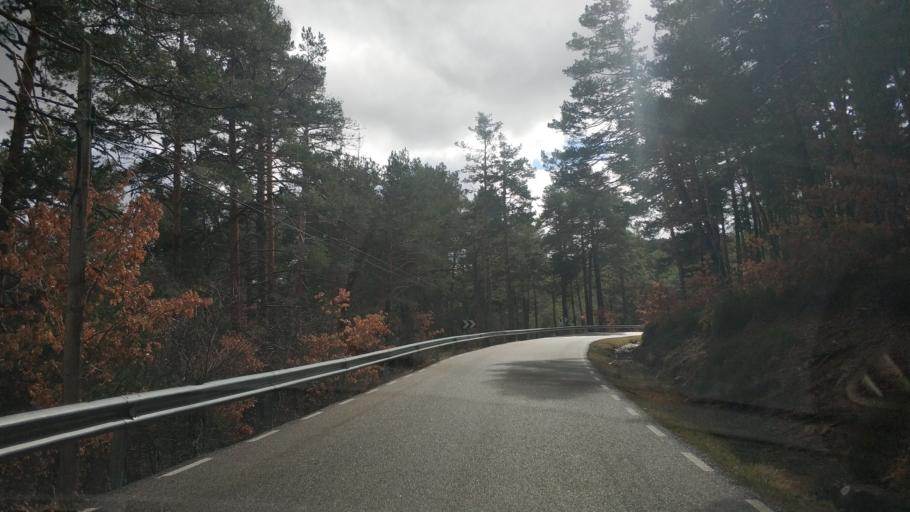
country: ES
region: Castille and Leon
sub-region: Provincia de Burgos
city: Quintanar de la Sierra
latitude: 42.0085
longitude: -3.0199
